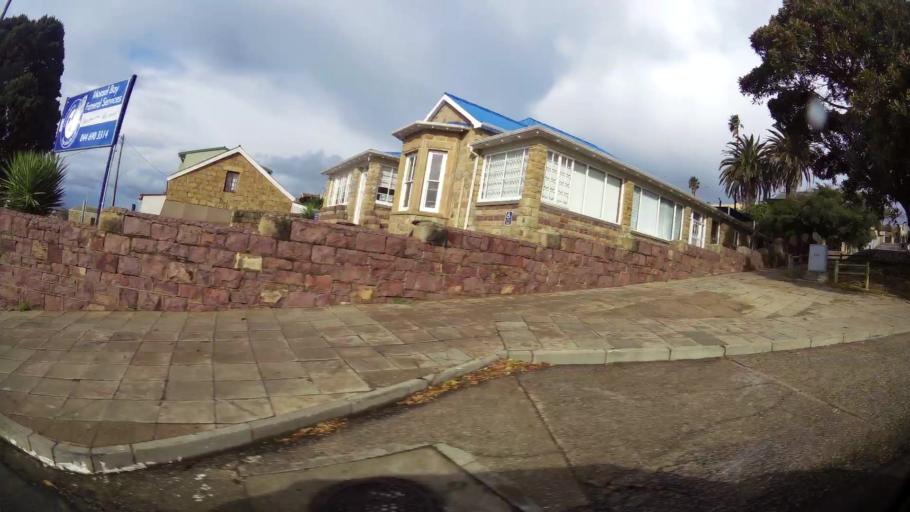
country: ZA
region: Western Cape
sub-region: Eden District Municipality
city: Mossel Bay
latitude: -34.1839
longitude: 22.1427
